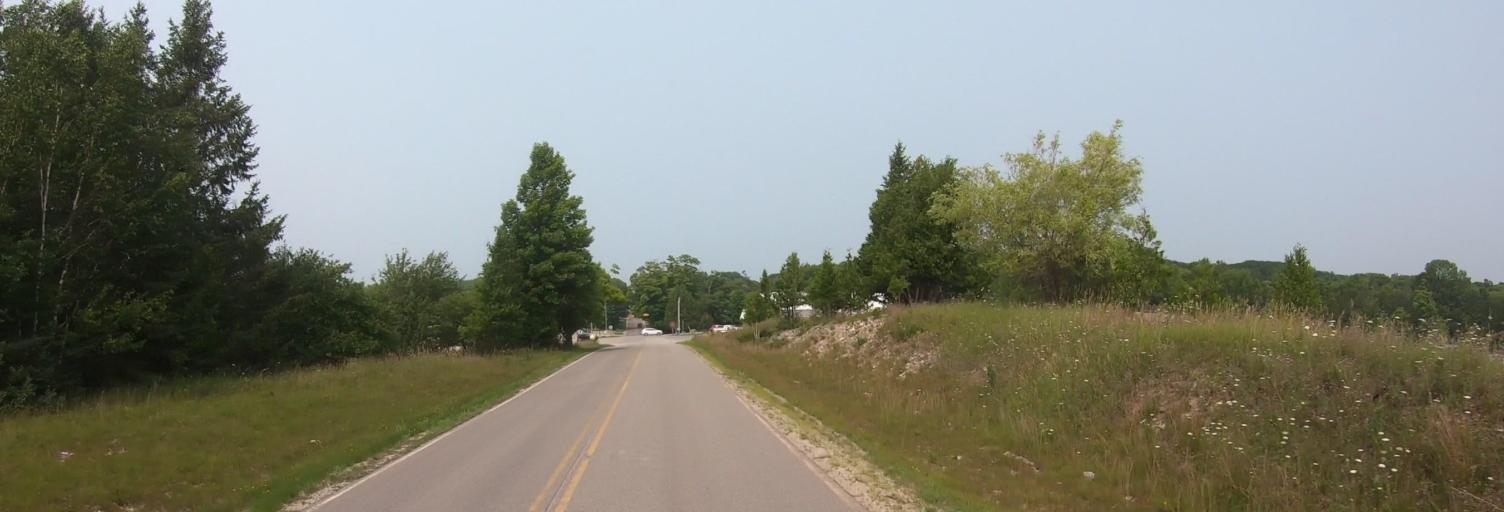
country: CA
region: Ontario
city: Thessalon
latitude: 45.9972
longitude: -83.7387
